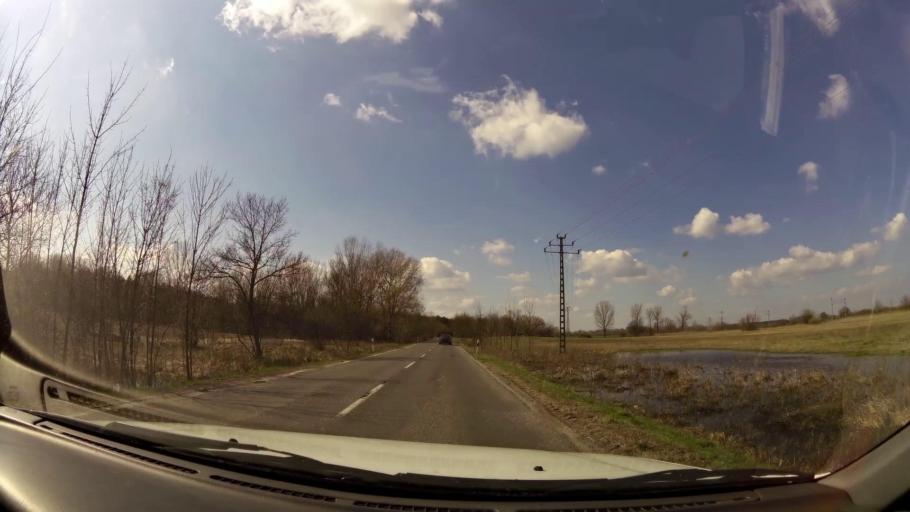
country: HU
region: Pest
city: Farmos
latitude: 47.3578
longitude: 19.8214
